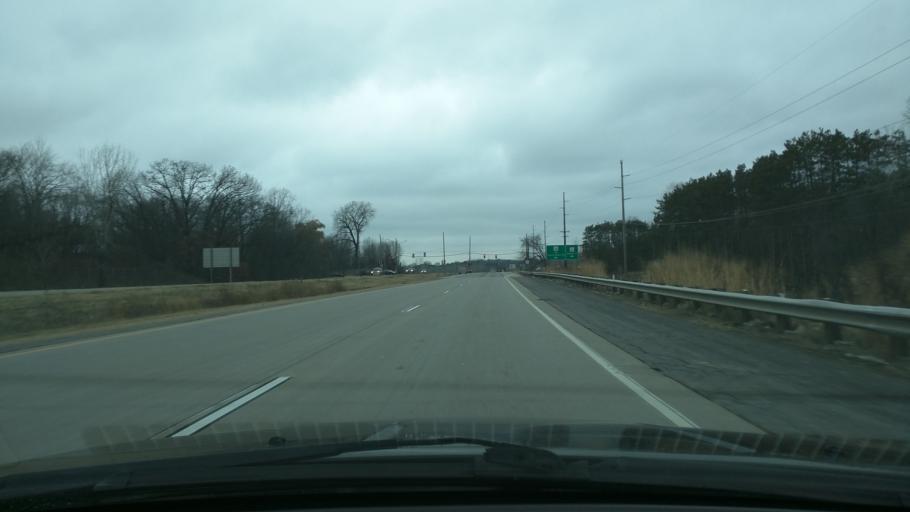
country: US
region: Minnesota
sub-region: Dakota County
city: Inver Grove Heights
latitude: 44.8380
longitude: -93.0982
